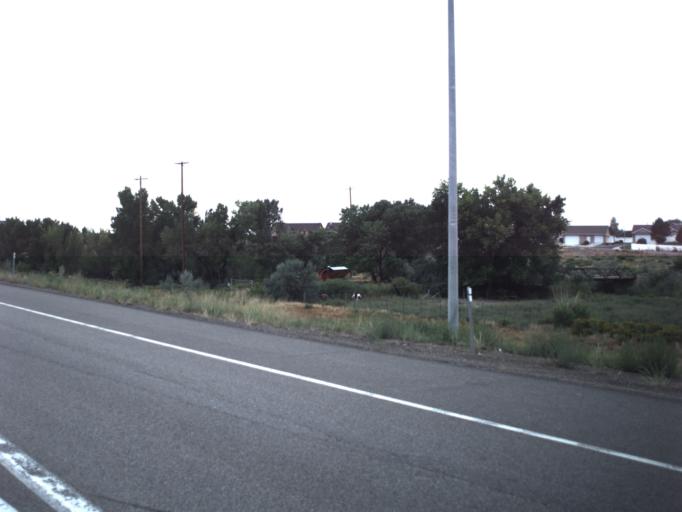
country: US
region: Utah
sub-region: Carbon County
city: Price
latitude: 39.5899
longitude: -110.8171
